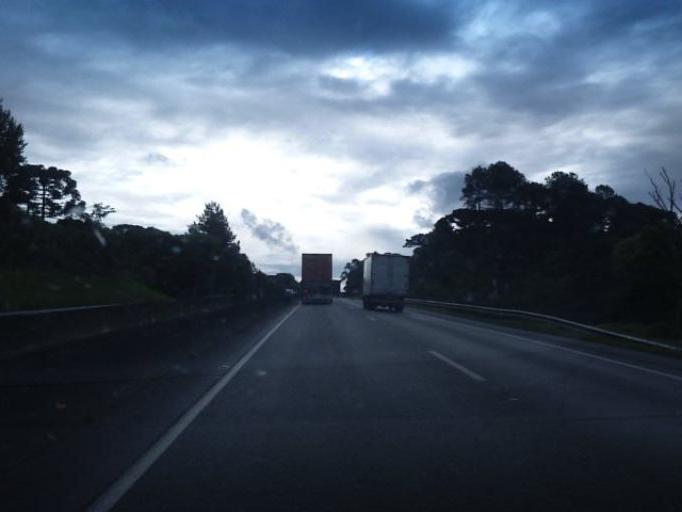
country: BR
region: Parana
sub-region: Campina Grande Do Sul
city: Campina Grande do Sul
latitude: -25.3068
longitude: -48.9767
